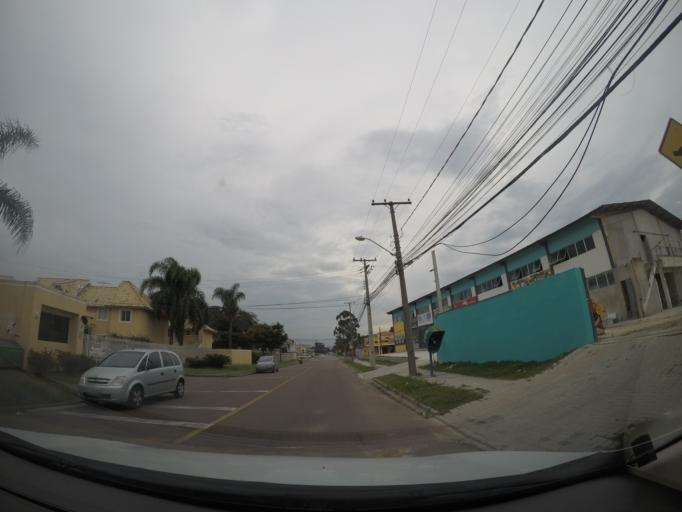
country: BR
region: Parana
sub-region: Curitiba
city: Curitiba
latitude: -25.4698
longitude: -49.2440
